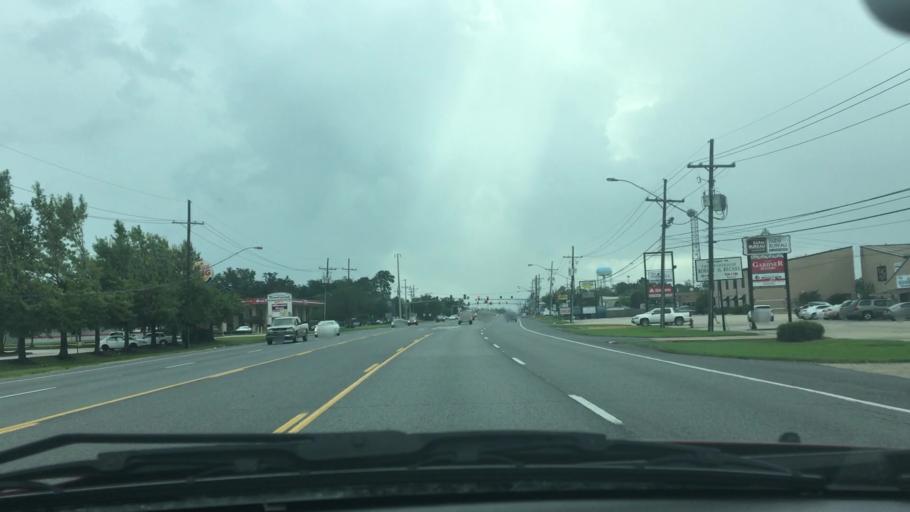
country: US
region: Louisiana
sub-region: Saint John the Baptist Parish
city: Laplace
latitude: 30.0684
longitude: -90.4836
